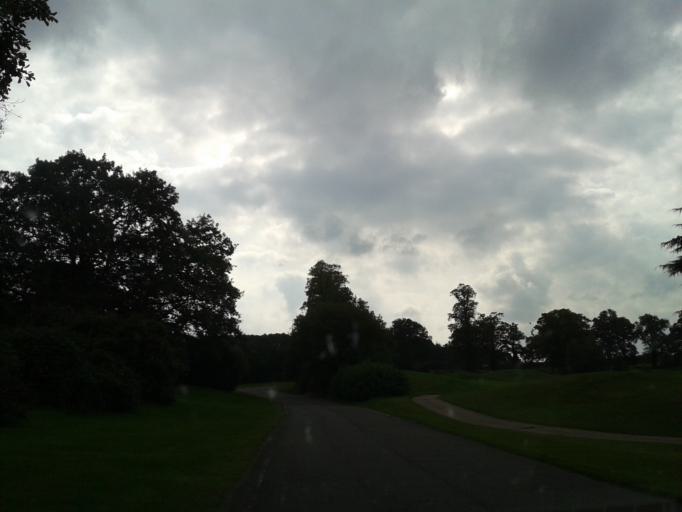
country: GB
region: England
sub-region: Warwickshire
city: Warwick
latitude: 52.3104
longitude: -1.5776
